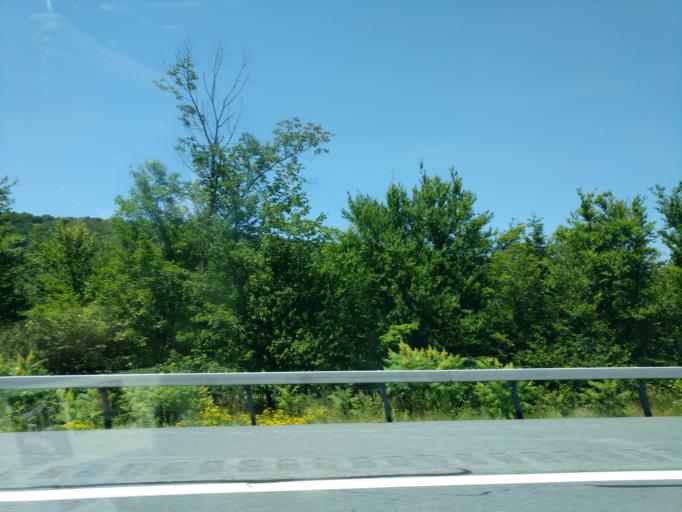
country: US
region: New York
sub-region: Sullivan County
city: Livingston Manor
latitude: 41.9261
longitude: -74.8524
